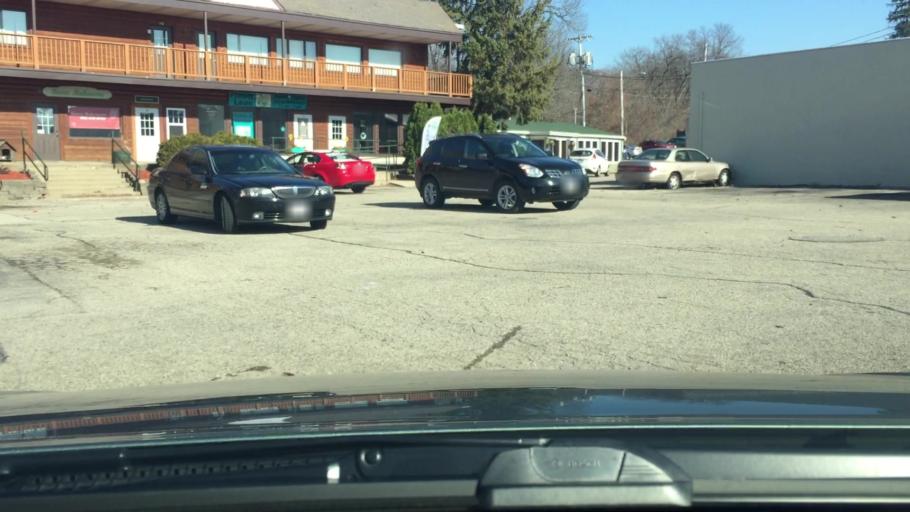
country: US
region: Wisconsin
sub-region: Jefferson County
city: Cambridge
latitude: 43.0042
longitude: -89.0193
